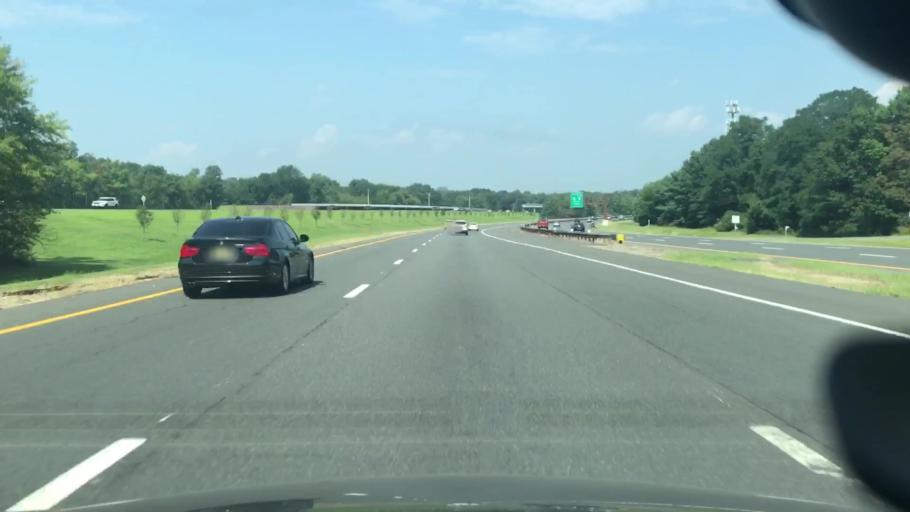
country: US
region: New Jersey
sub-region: Monmouth County
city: Strathmore
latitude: 40.4034
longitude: -74.1934
